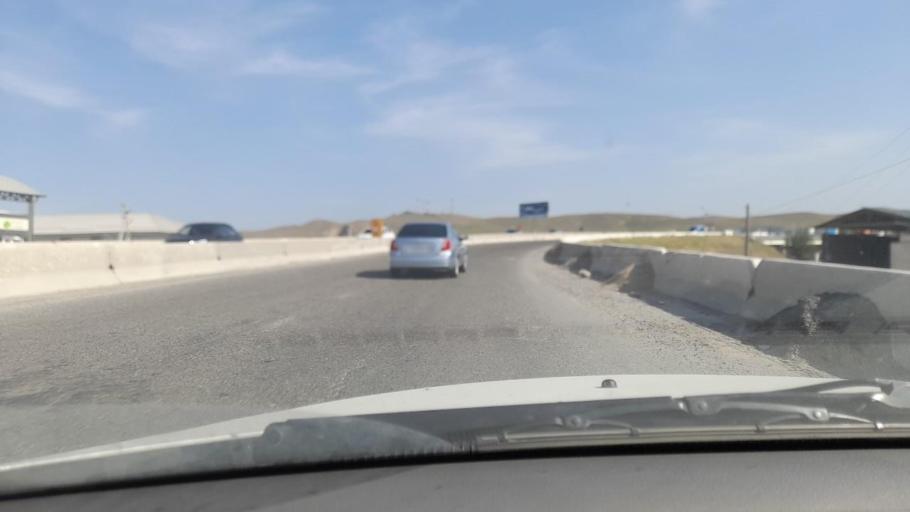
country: UZ
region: Samarqand
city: Samarqand
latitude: 39.6998
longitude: 67.0180
